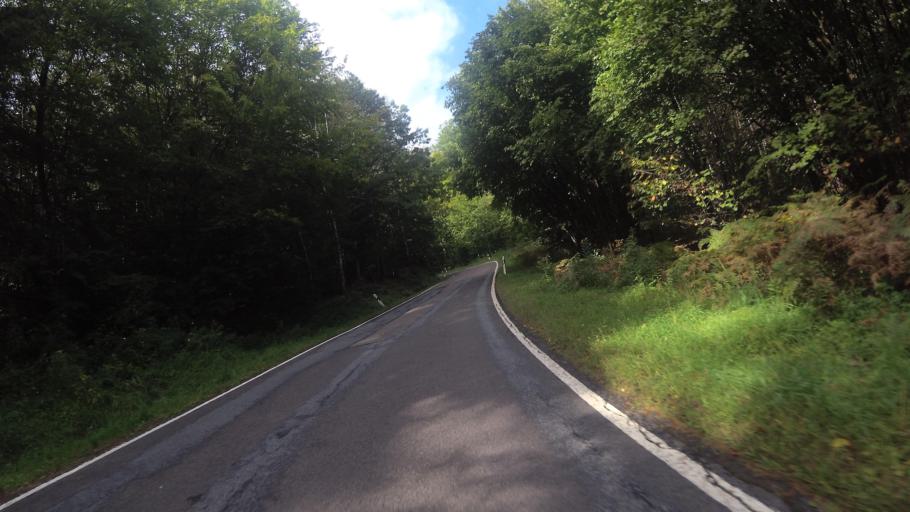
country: FR
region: Lorraine
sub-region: Departement de la Moselle
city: Freyming-Merlebach
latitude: 49.1732
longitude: 6.7987
